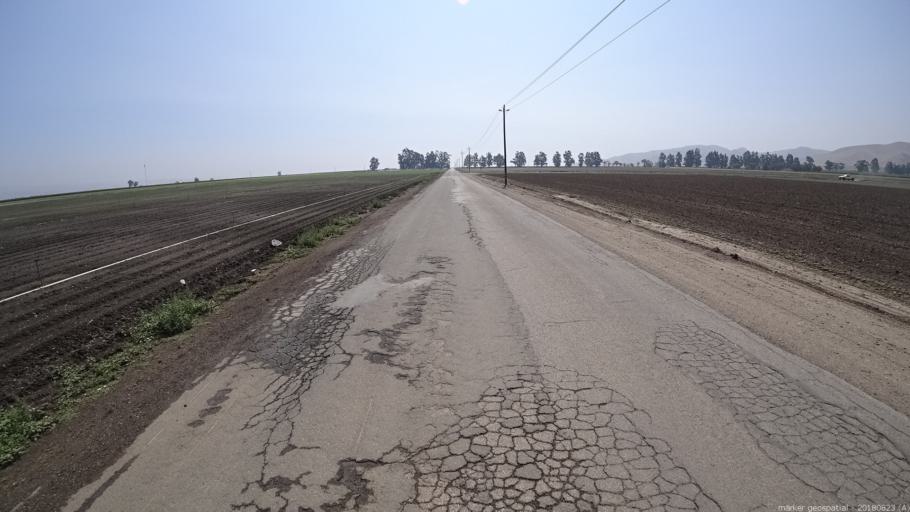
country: US
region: California
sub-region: Monterey County
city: Greenfield
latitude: 36.2817
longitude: -121.2328
